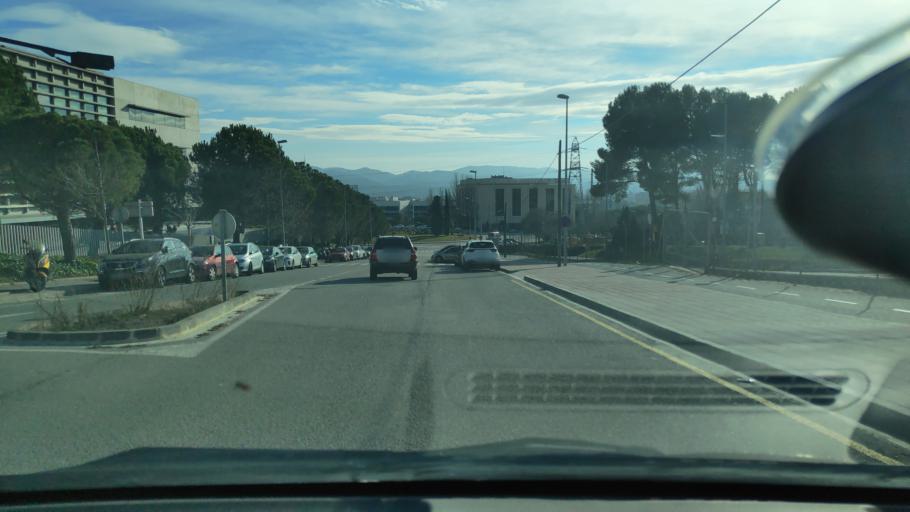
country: ES
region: Catalonia
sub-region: Provincia de Barcelona
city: Sant Cugat del Valles
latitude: 41.4943
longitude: 2.0739
